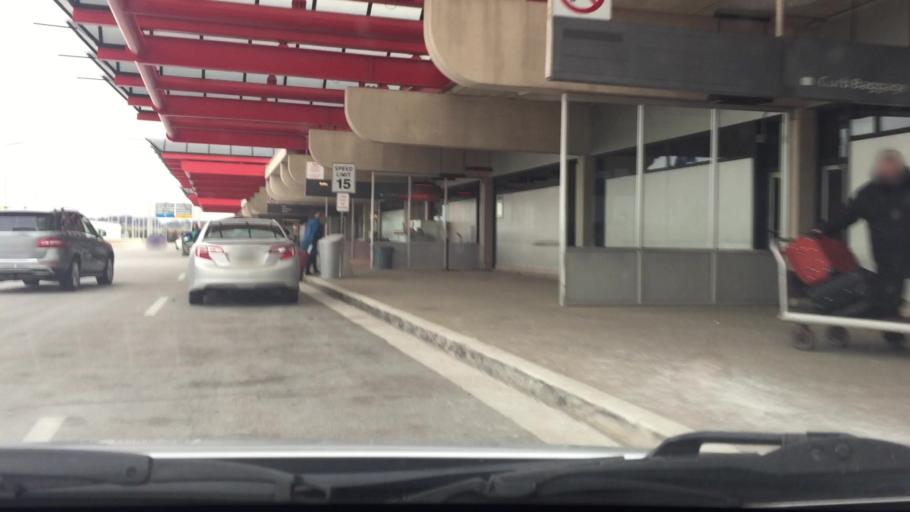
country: US
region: Pennsylvania
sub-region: Allegheny County
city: Carnot-Moon
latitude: 40.4954
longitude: -80.2566
